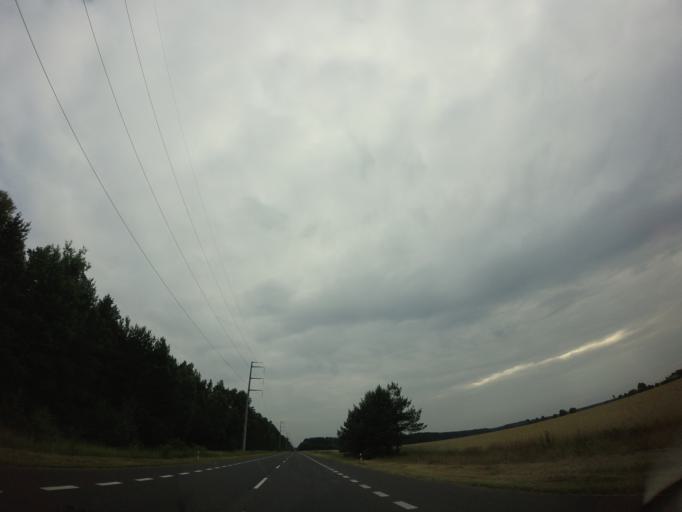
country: PL
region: West Pomeranian Voivodeship
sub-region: Powiat walecki
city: Miroslawiec
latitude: 53.3913
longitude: 16.1667
